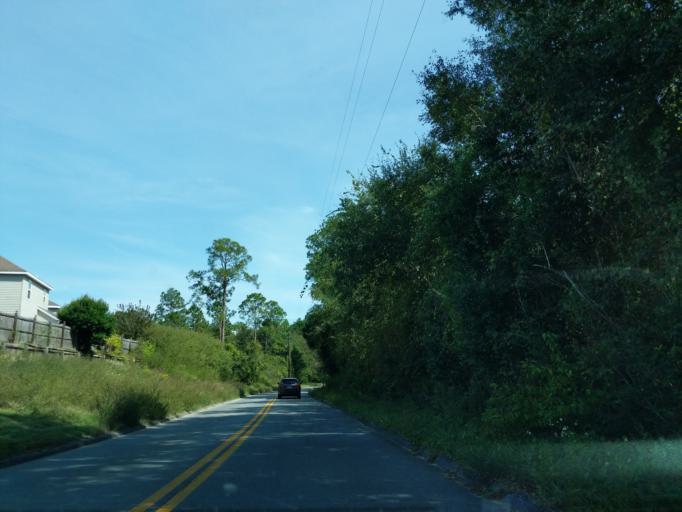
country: US
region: Florida
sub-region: Okaloosa County
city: Crestview
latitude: 30.7037
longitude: -86.5824
